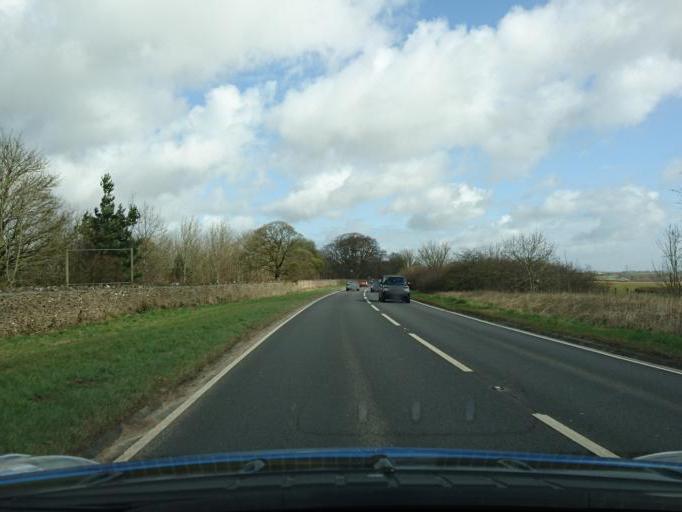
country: GB
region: England
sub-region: South Gloucestershire
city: Cold Ashton
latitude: 51.4739
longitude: -2.3646
